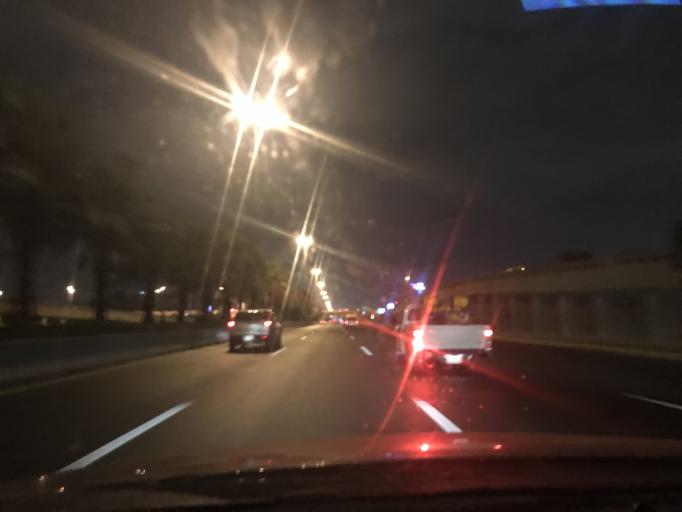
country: SA
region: Ar Riyad
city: Riyadh
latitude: 24.7467
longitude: 46.6137
